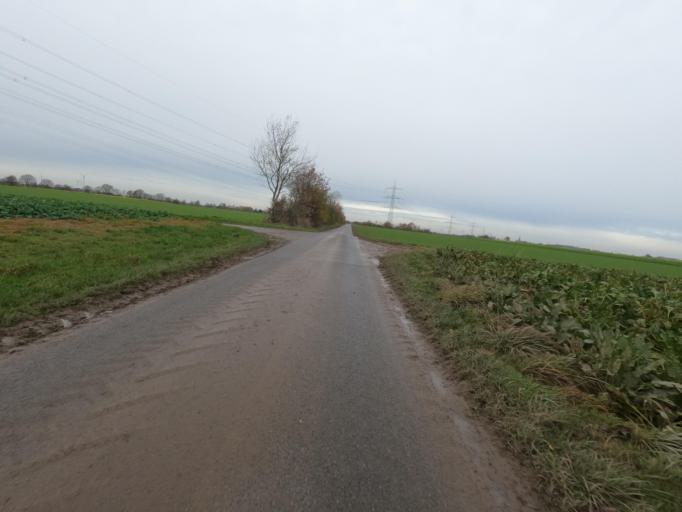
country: DE
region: North Rhine-Westphalia
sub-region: Regierungsbezirk Koln
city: Heinsberg
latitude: 51.0348
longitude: 6.1153
